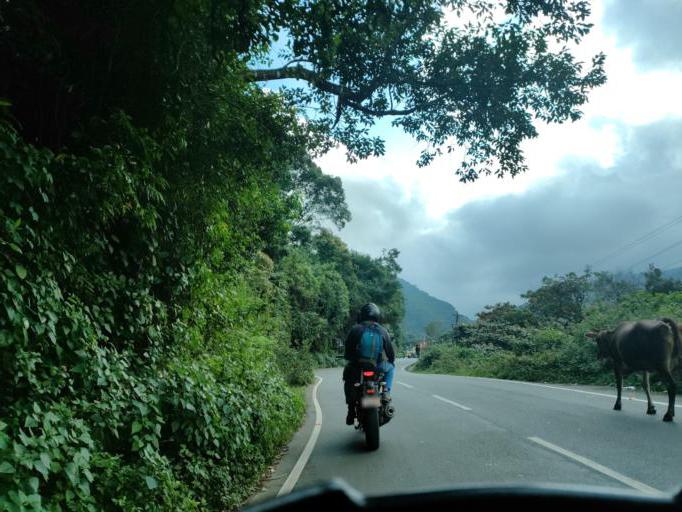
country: IN
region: Tamil Nadu
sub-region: Dindigul
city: Kodaikanal
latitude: 10.2630
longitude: 77.5376
